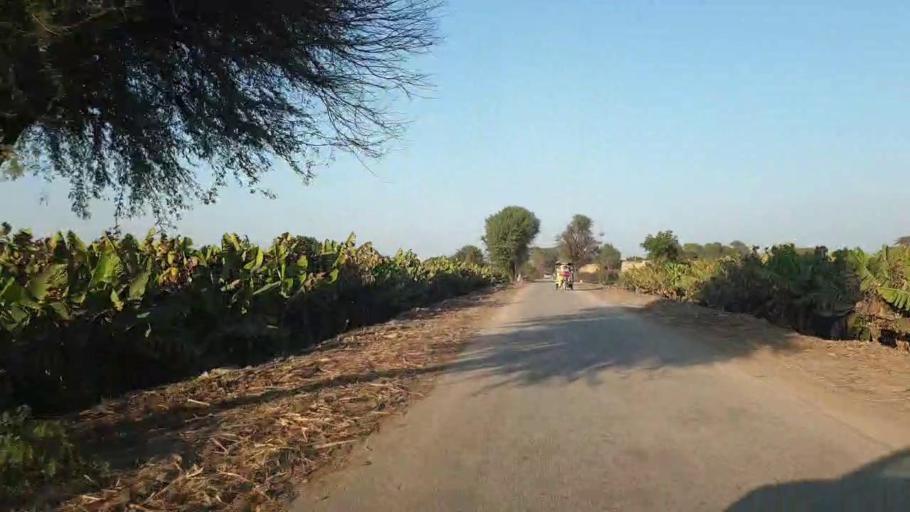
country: PK
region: Sindh
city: Tando Allahyar
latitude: 25.3665
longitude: 68.7434
